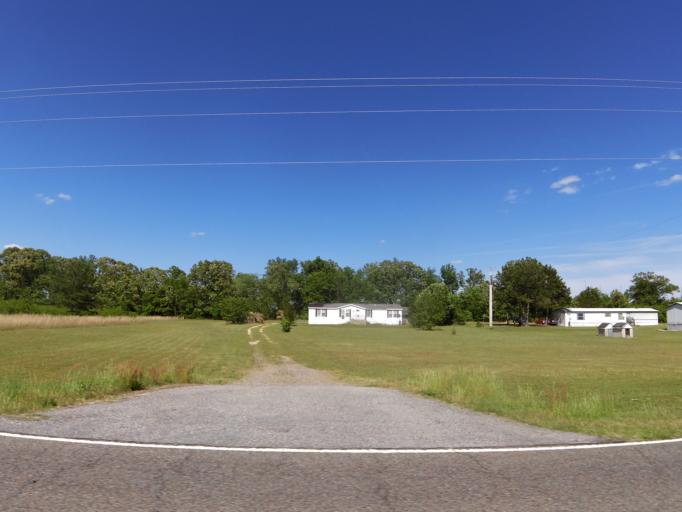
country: US
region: South Carolina
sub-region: Barnwell County
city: Williston
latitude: 33.4579
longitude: -81.4967
